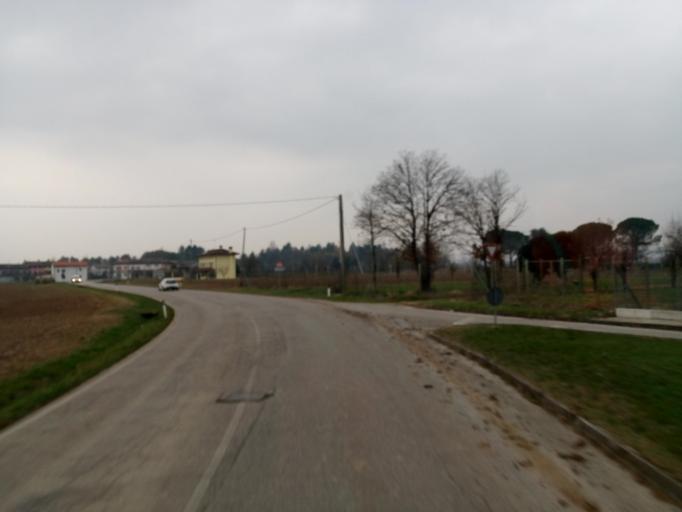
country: IT
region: Friuli Venezia Giulia
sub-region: Provincia di Udine
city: Faedis
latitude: 46.1298
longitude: 13.3324
